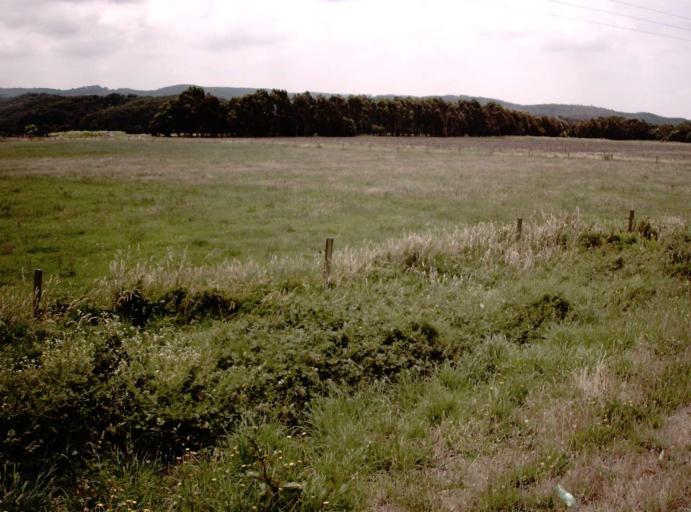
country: AU
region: Victoria
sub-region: Latrobe
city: Traralgon
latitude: -38.5045
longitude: 146.6649
